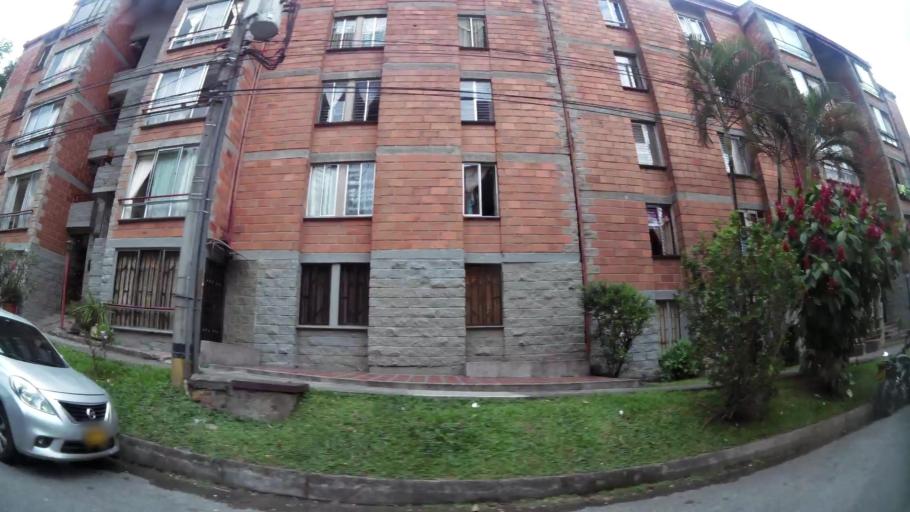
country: CO
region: Antioquia
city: Envigado
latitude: 6.1589
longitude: -75.5966
